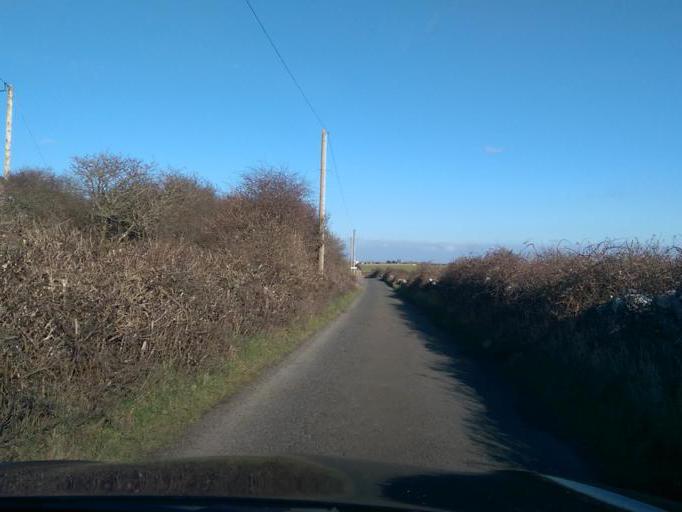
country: IE
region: Connaught
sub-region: County Galway
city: Oranmore
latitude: 53.2236
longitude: -8.9361
